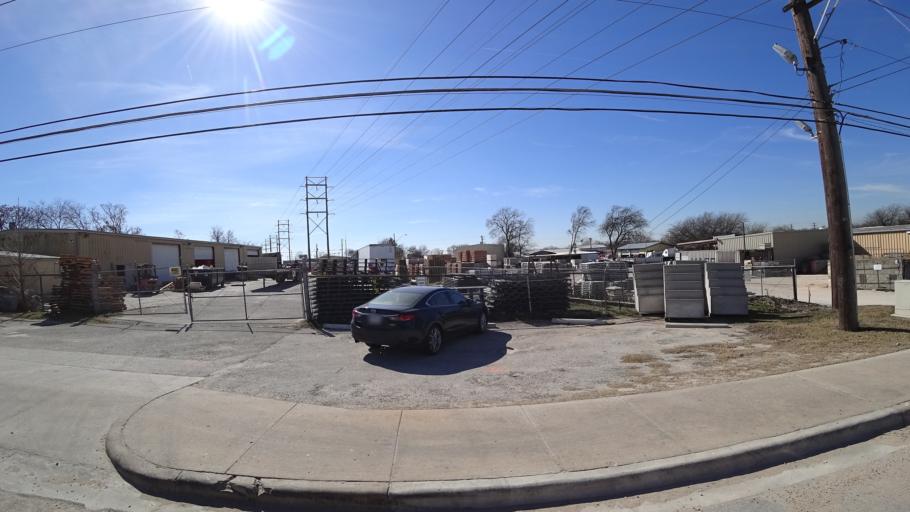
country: US
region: Texas
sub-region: Travis County
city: Wells Branch
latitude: 30.3801
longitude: -97.6890
